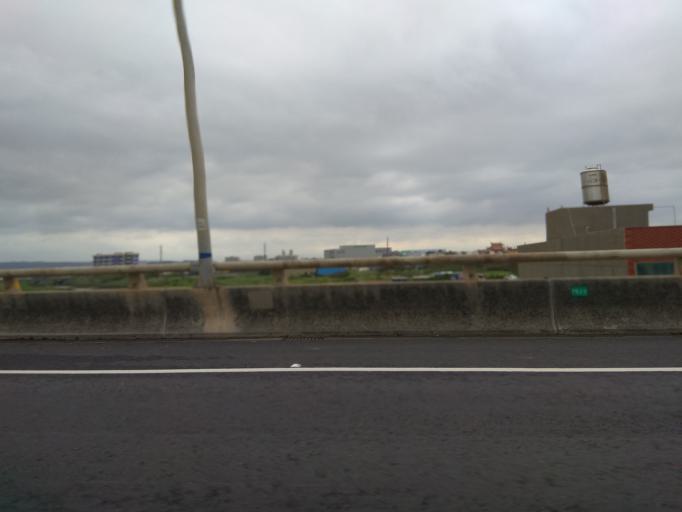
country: TW
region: Taiwan
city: Taoyuan City
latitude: 25.1122
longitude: 121.2421
